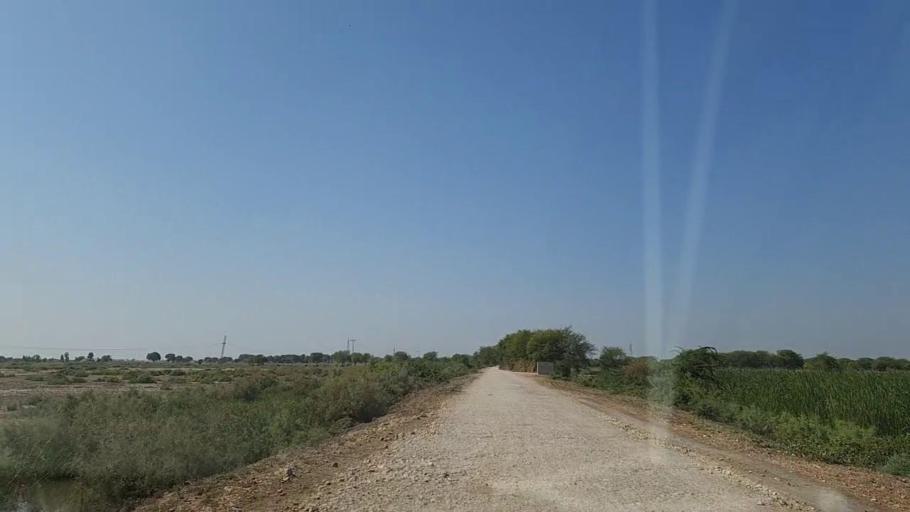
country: PK
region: Sindh
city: Chuhar Jamali
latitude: 24.4164
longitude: 68.0319
